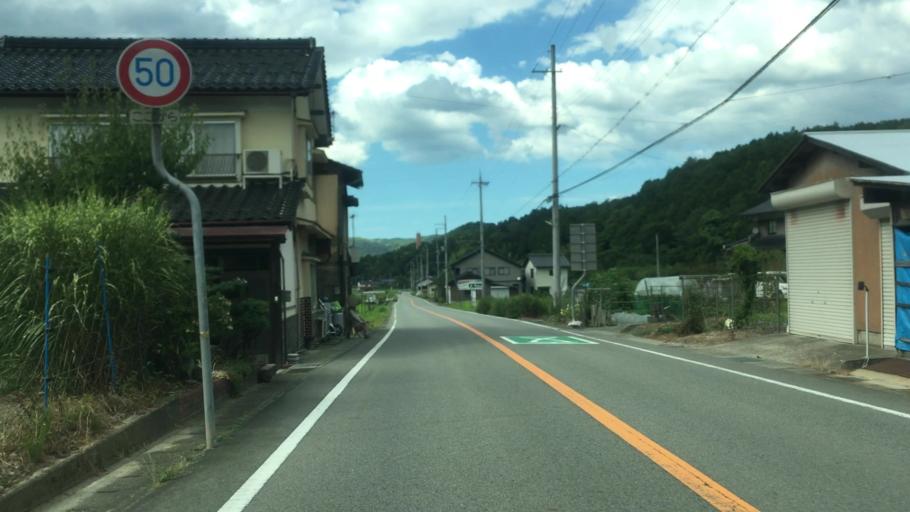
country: JP
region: Hyogo
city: Toyooka
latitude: 35.5358
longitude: 134.7897
